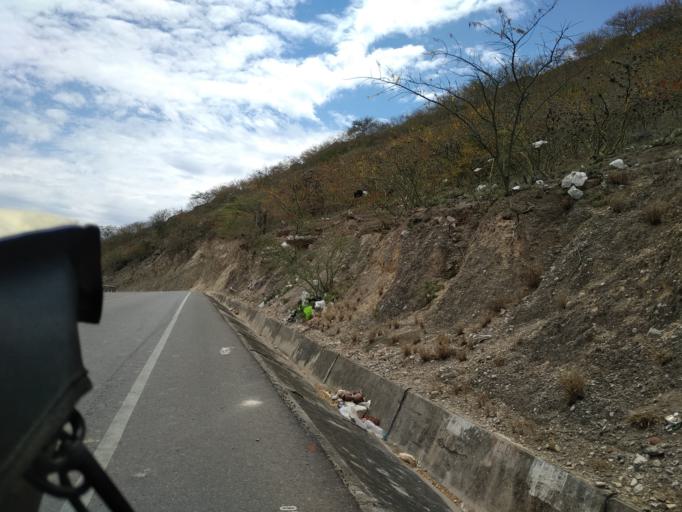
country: PE
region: Cajamarca
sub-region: Provincia de Jaen
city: Bellavista
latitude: -5.7425
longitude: -78.6575
